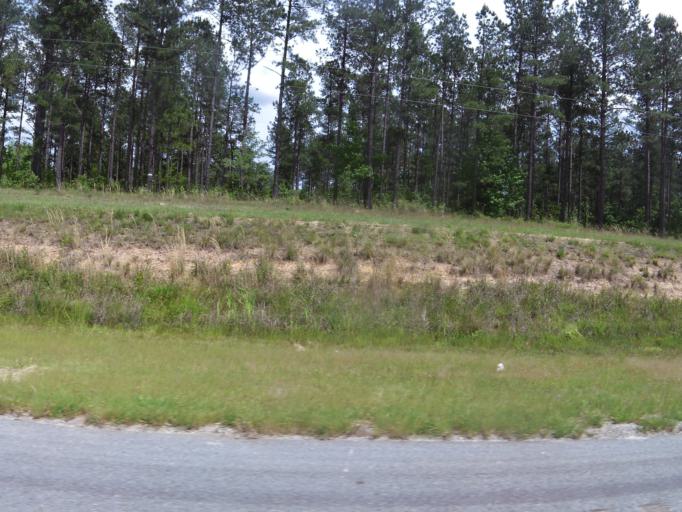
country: US
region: Georgia
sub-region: Emanuel County
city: Swainsboro
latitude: 32.7097
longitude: -82.3910
